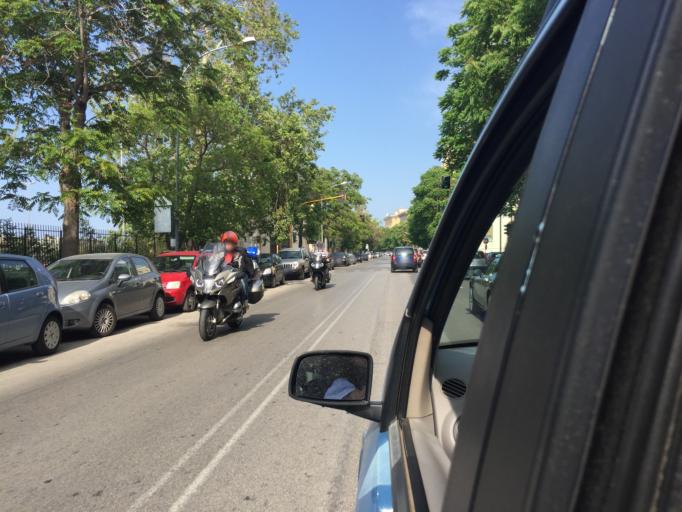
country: IT
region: Apulia
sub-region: Provincia di Bari
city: Bari
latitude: 41.1282
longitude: 16.8571
